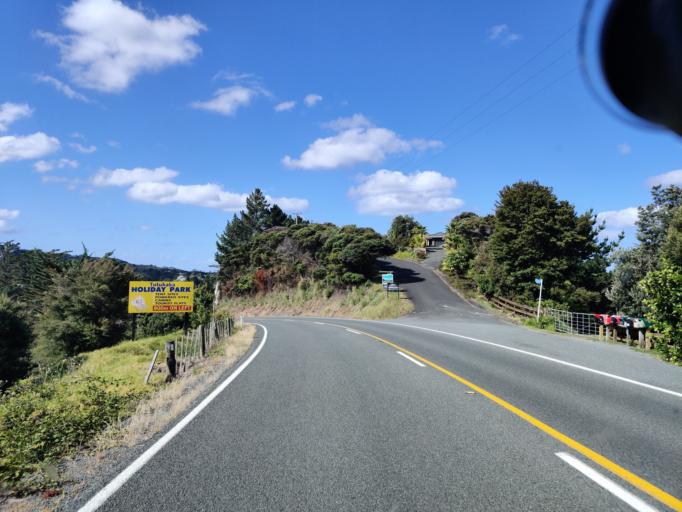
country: NZ
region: Northland
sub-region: Whangarei
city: Ngunguru
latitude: -35.6157
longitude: 174.5206
